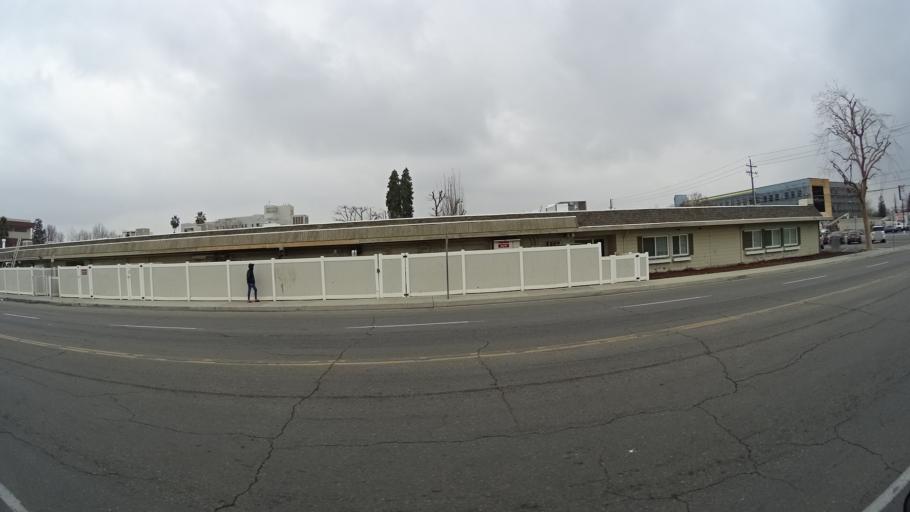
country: US
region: California
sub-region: Kern County
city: Bakersfield
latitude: 35.3911
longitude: -119.0106
